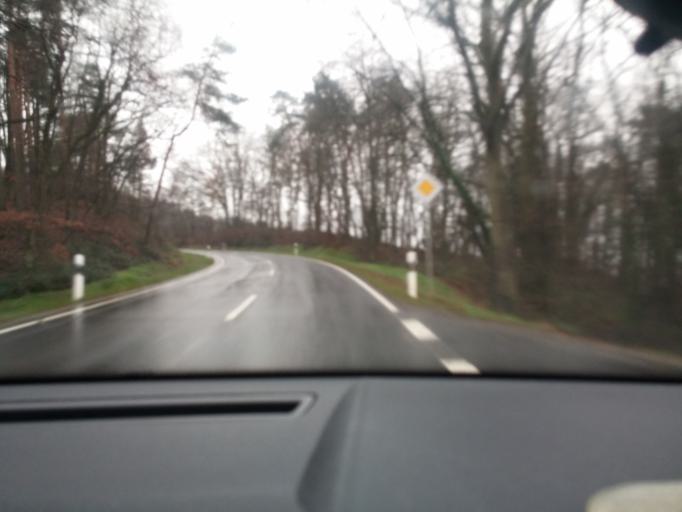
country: DE
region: Hesse
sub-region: Regierungsbezirk Darmstadt
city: Brensbach
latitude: 49.7605
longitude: 8.8991
